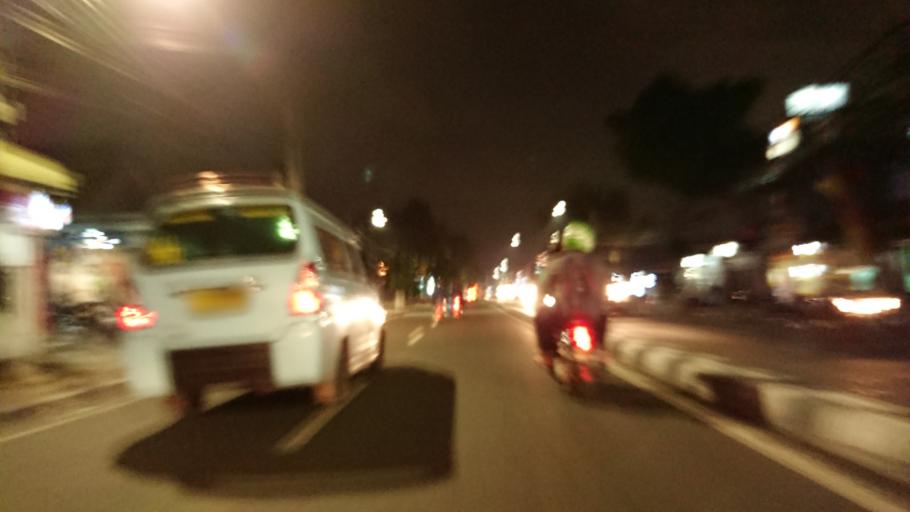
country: ID
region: Jakarta Raya
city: Jakarta
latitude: -6.1943
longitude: 106.8052
